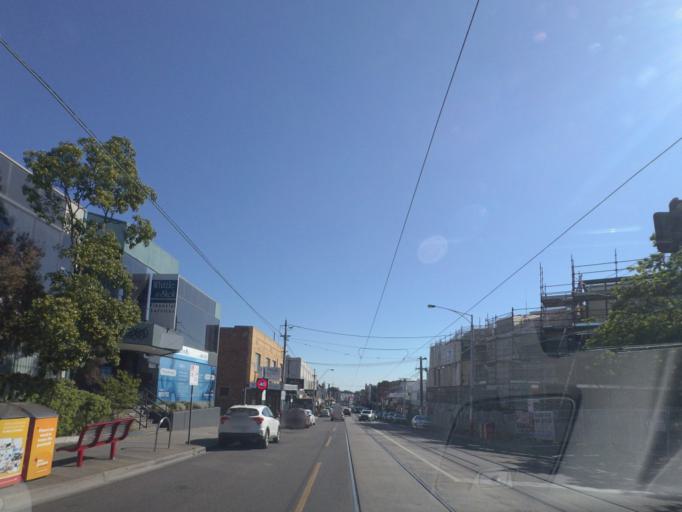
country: AU
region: Victoria
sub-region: Boroondara
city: Kew
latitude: -37.8056
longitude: 145.0342
